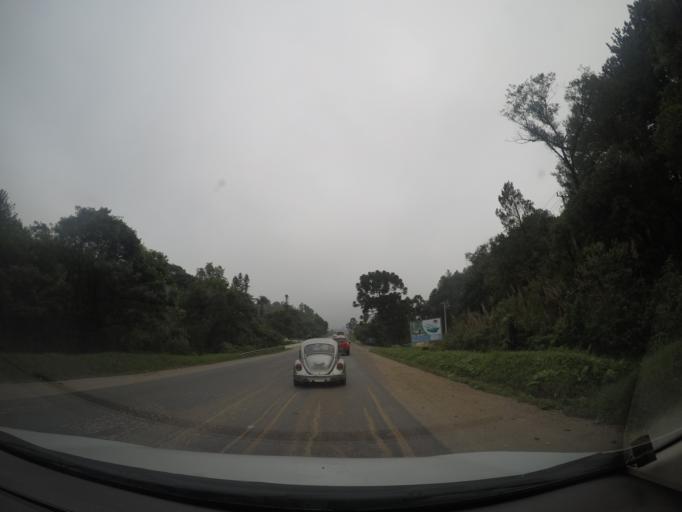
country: BR
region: Parana
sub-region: Almirante Tamandare
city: Almirante Tamandare
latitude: -25.3274
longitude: -49.2951
